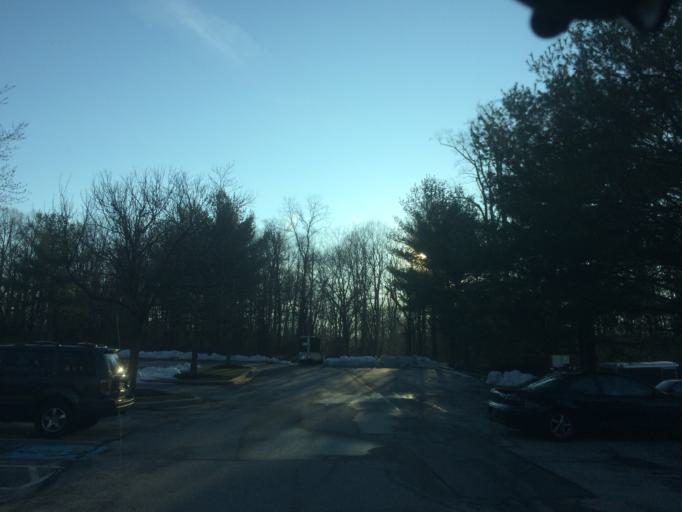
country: US
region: Maryland
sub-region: Howard County
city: Riverside
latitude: 39.1947
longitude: -76.8525
